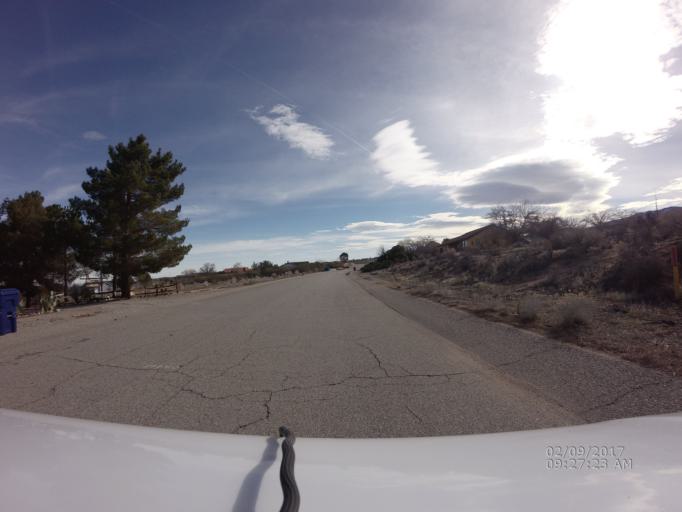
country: US
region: California
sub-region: Los Angeles County
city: Lake Los Angeles
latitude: 34.4727
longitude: -117.8383
